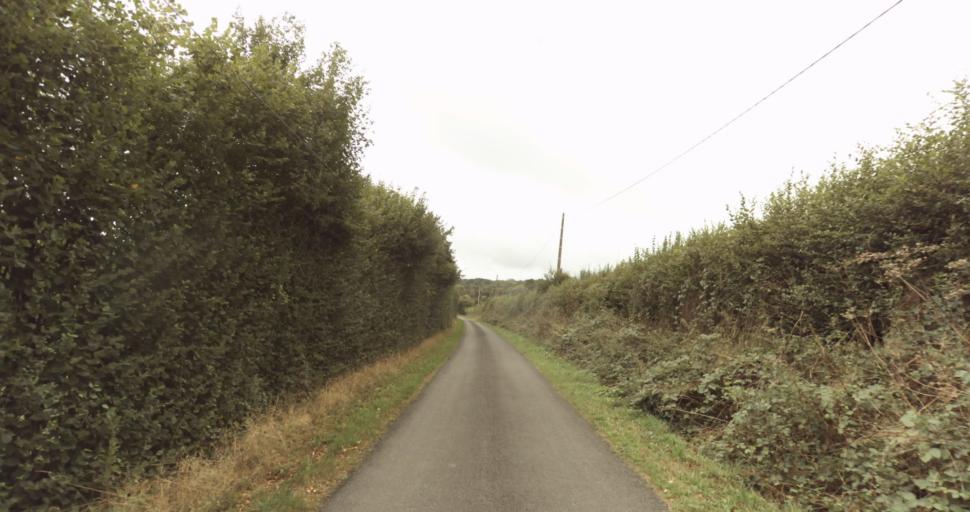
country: FR
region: Lower Normandy
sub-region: Departement de l'Orne
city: Gace
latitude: 48.8547
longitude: 0.2839
